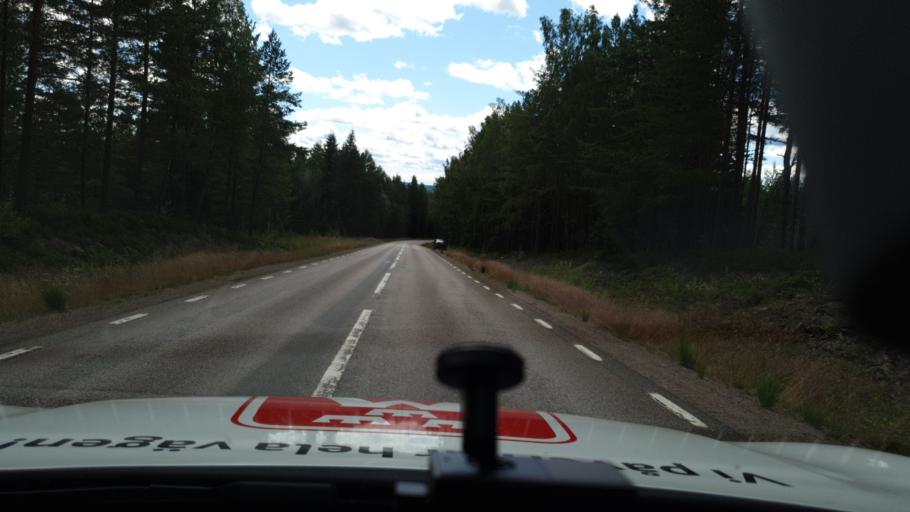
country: SE
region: Vaermland
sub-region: Sunne Kommun
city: Sunne
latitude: 59.6853
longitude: 13.0479
